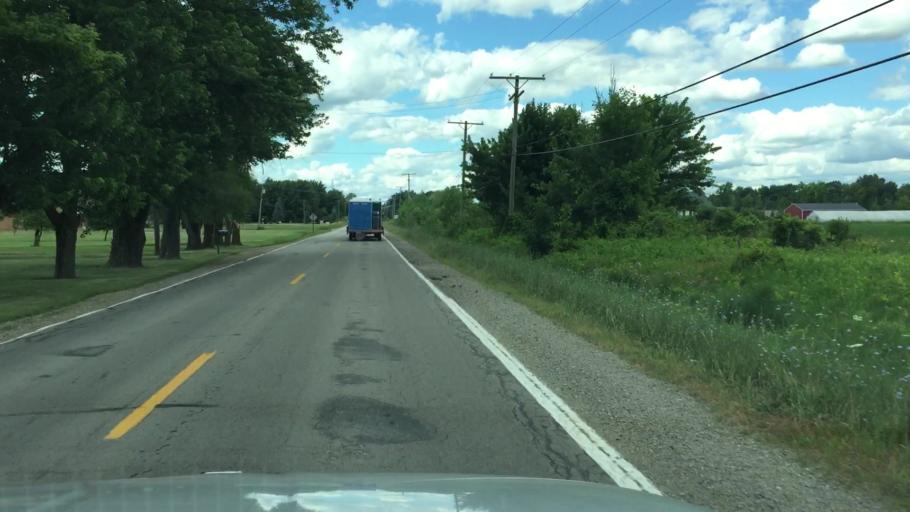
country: US
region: Michigan
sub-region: Macomb County
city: Armada
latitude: 42.9102
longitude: -82.9454
